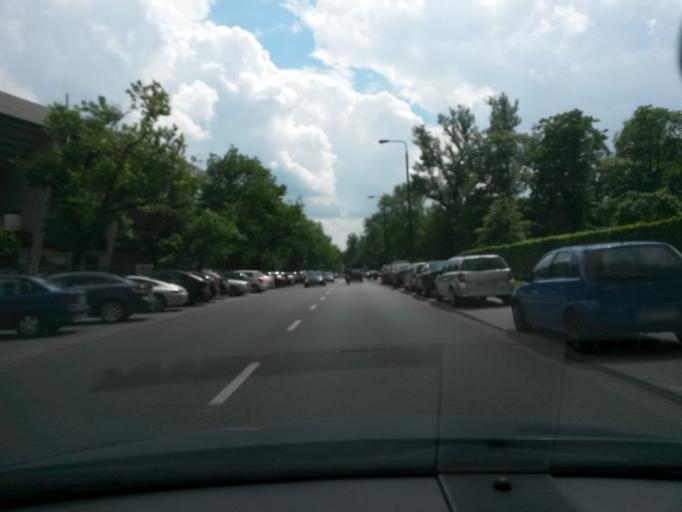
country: PL
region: Masovian Voivodeship
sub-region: Warszawa
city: Srodmiescie
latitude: 52.2203
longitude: 21.0364
